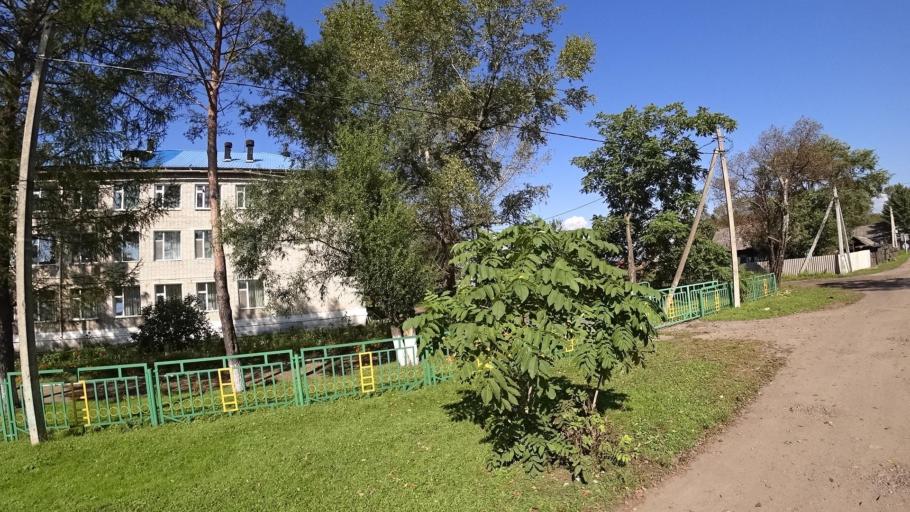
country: RU
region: Jewish Autonomous Oblast
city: Bira
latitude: 48.9975
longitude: 132.4553
